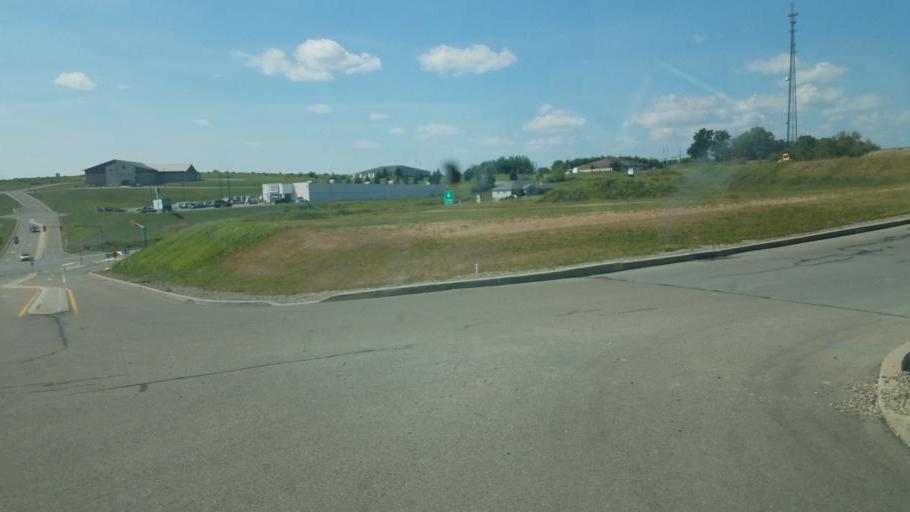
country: US
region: Pennsylvania
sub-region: Clarion County
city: Clarion
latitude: 41.1804
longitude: -79.3935
